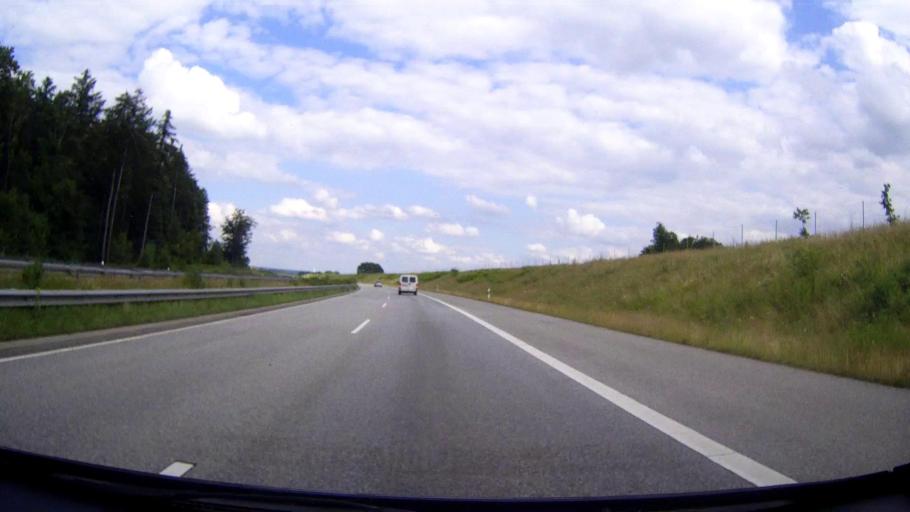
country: DE
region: Schleswig-Holstein
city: Strukdorf
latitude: 53.9161
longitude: 10.5092
